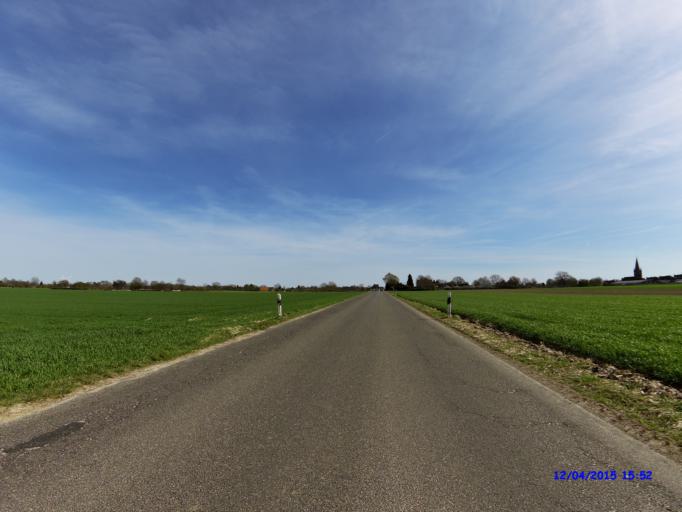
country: DE
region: North Rhine-Westphalia
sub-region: Regierungsbezirk Koln
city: Ubach-Palenberg
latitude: 50.9348
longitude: 6.0678
